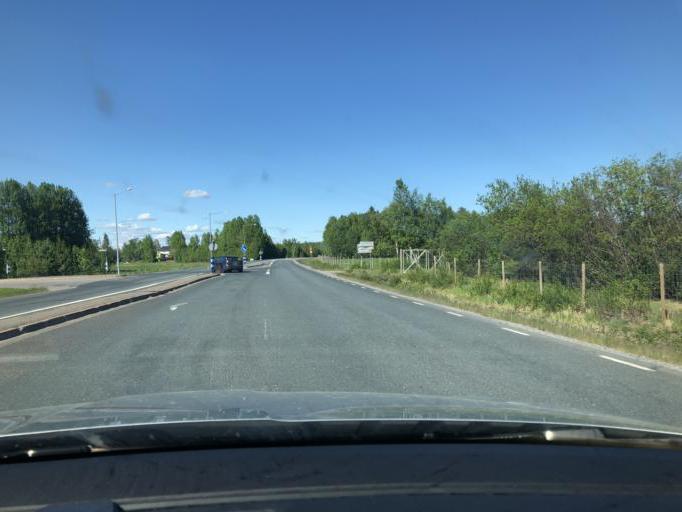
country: SE
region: Norrbotten
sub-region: Kalix Kommun
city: Kalix
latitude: 65.8414
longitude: 23.1939
